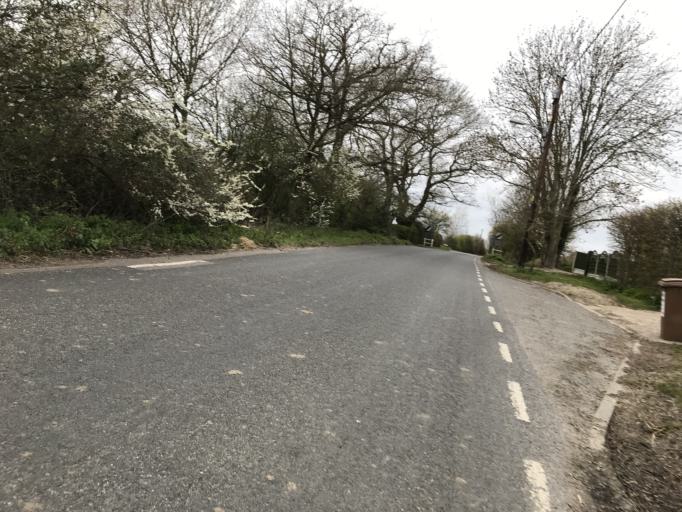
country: GB
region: England
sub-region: Essex
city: Stock
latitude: 51.6734
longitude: 0.4855
